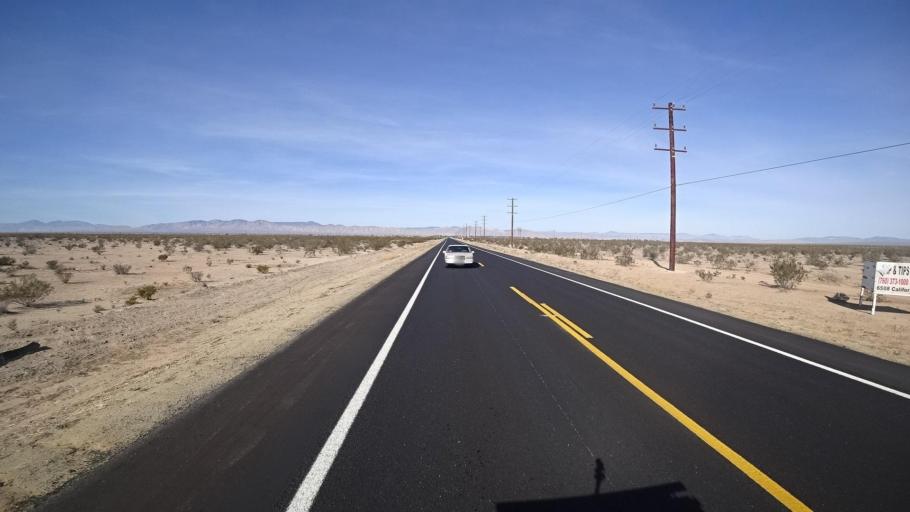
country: US
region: California
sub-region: Kern County
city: California City
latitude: 35.1045
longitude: -117.9209
